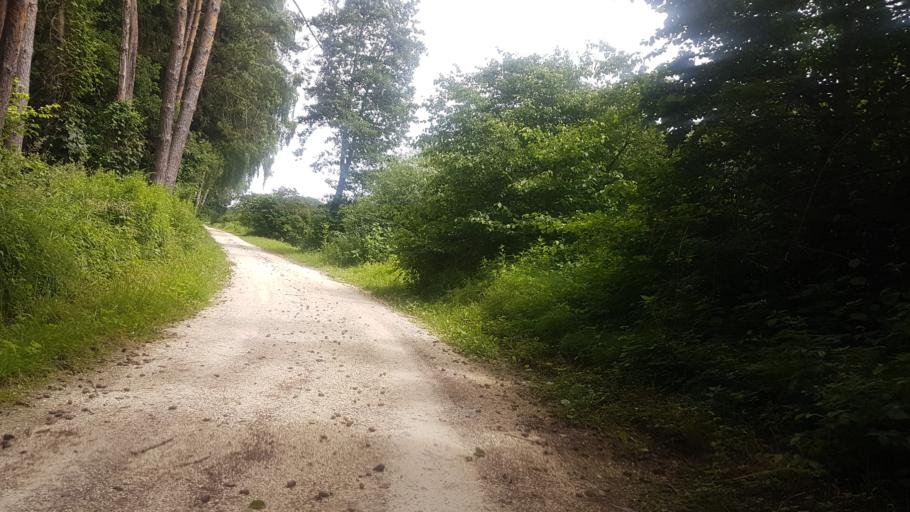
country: DE
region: Bavaria
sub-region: Swabia
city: Dillingen an der Donau
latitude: 48.5758
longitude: 10.5235
